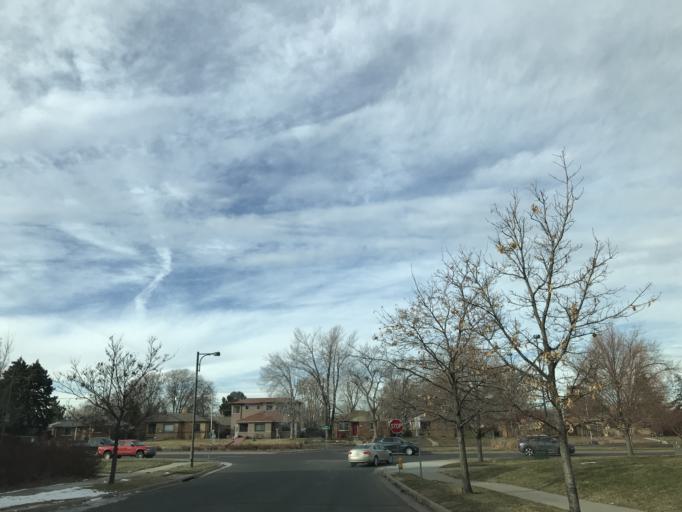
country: US
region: Colorado
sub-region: Adams County
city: Commerce City
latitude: 39.7594
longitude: -104.9025
